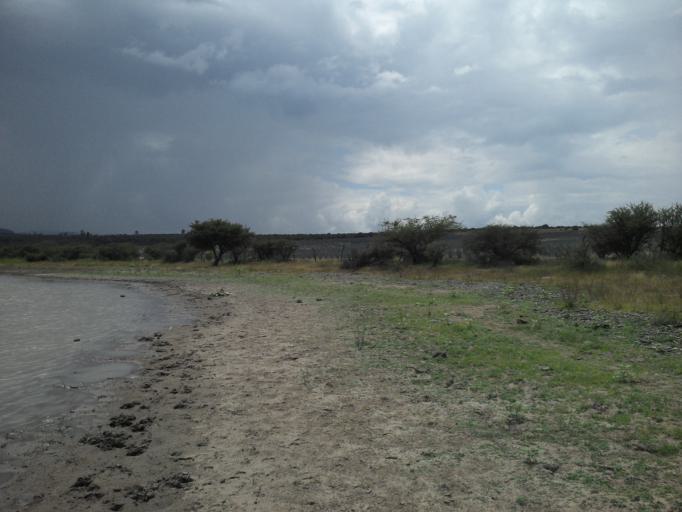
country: MX
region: Guanajuato
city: Ciudad Manuel Doblado
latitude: 20.8079
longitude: -102.0058
